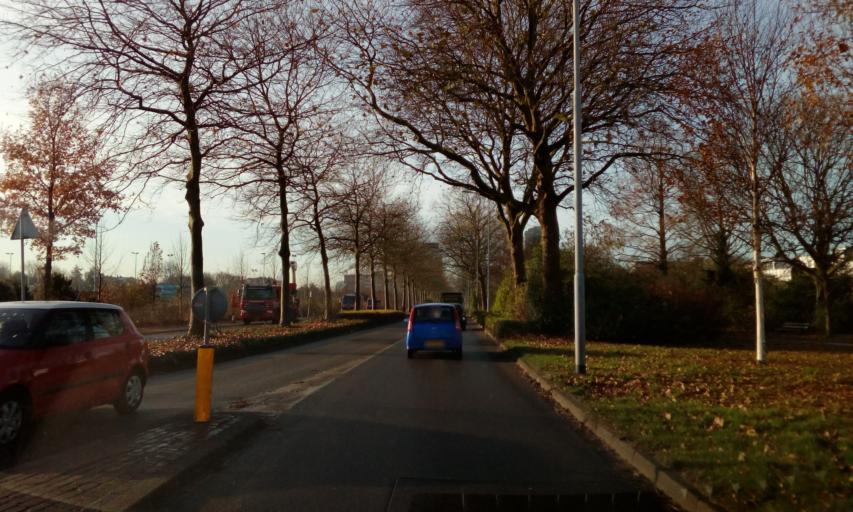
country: NL
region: South Holland
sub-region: Gemeente Leidschendam-Voorburg
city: Voorburg
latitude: 52.0783
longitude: 4.3677
